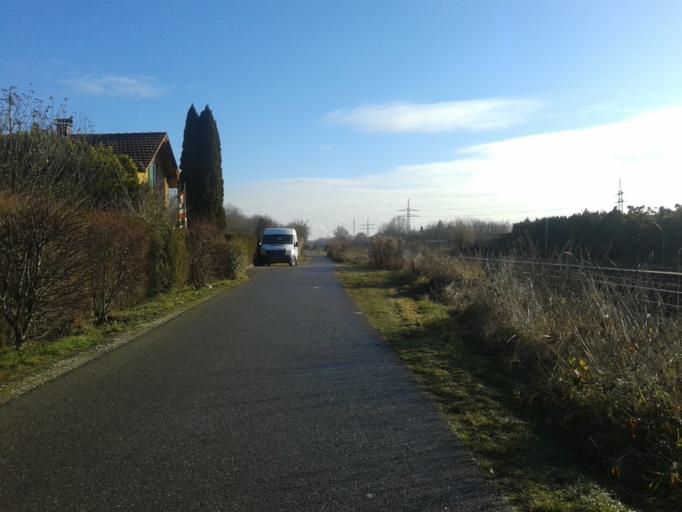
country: DE
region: Baden-Wuerttemberg
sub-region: Tuebingen Region
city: Ulm
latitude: 48.4080
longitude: 9.9335
